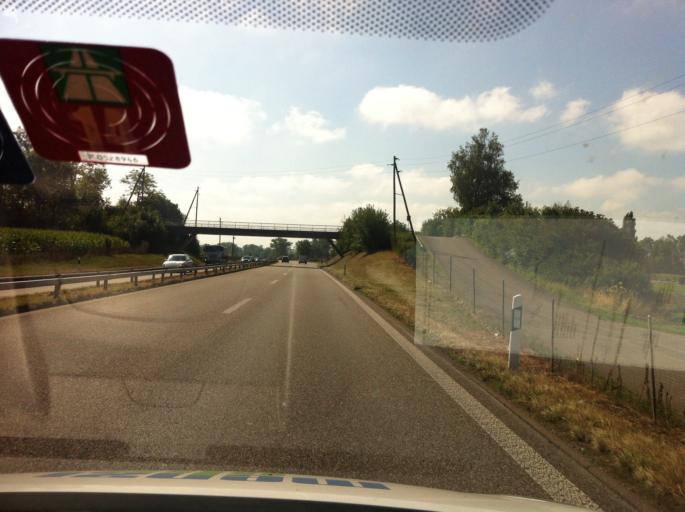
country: CH
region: Zurich
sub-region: Bezirk Buelach
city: Bachenbulach
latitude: 47.4758
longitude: 8.5537
